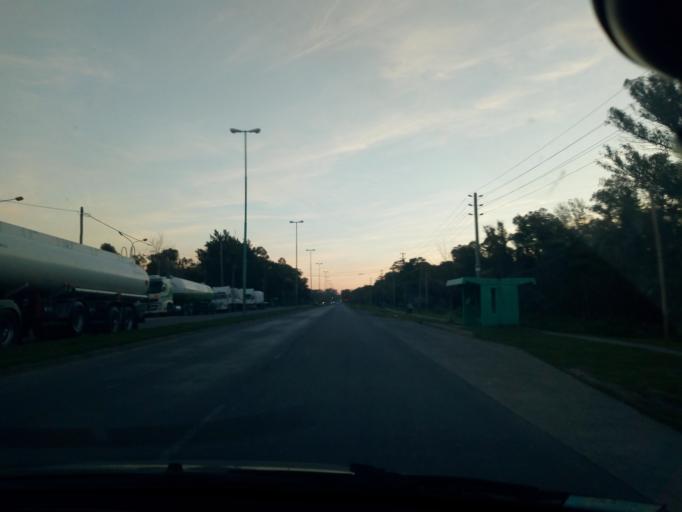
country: AR
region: Buenos Aires
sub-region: Partido de Ensenada
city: Ensenada
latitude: -34.8843
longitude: -57.9278
